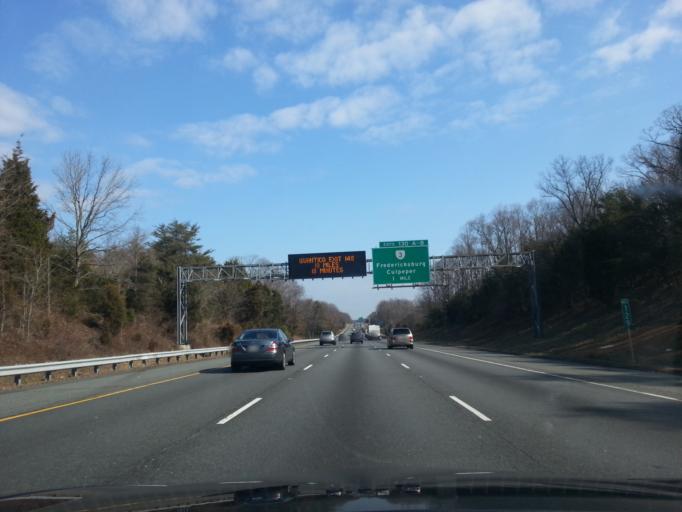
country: US
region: Virginia
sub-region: City of Fredericksburg
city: Fredericksburg
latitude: 38.2771
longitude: -77.5119
